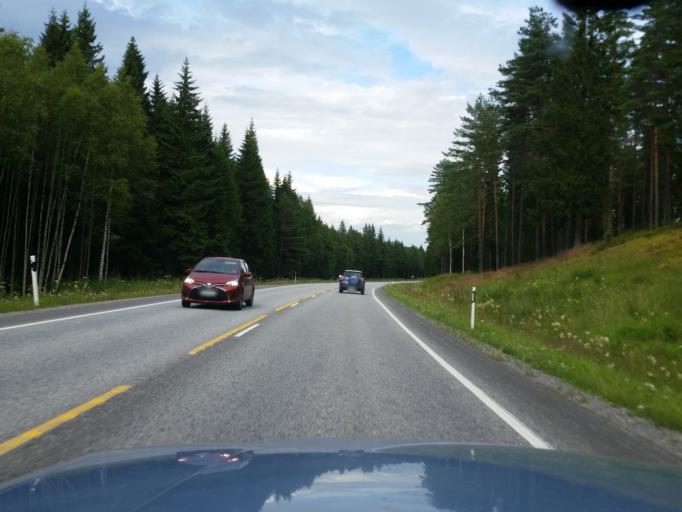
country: FI
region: Uusimaa
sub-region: Raaseporin
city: Karis
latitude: 60.0347
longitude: 23.5980
